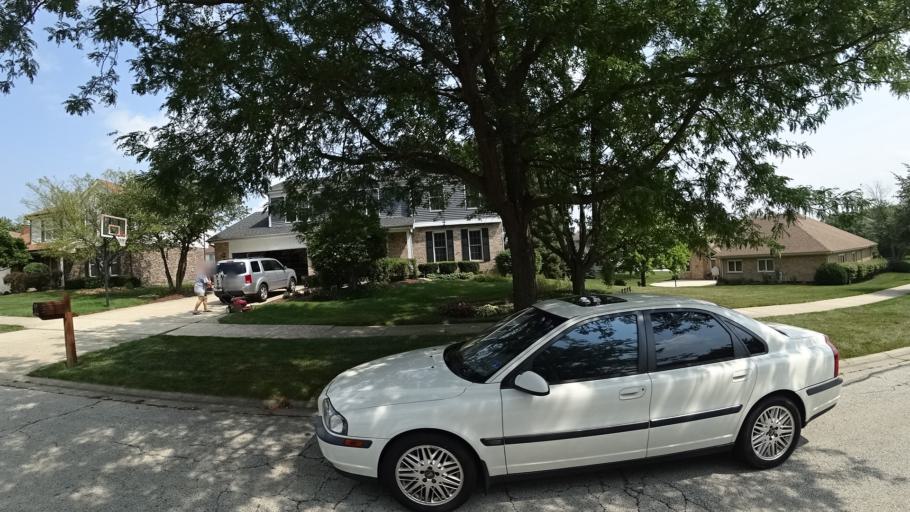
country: US
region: Illinois
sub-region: Will County
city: Goodings Grove
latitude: 41.6331
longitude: -87.8990
